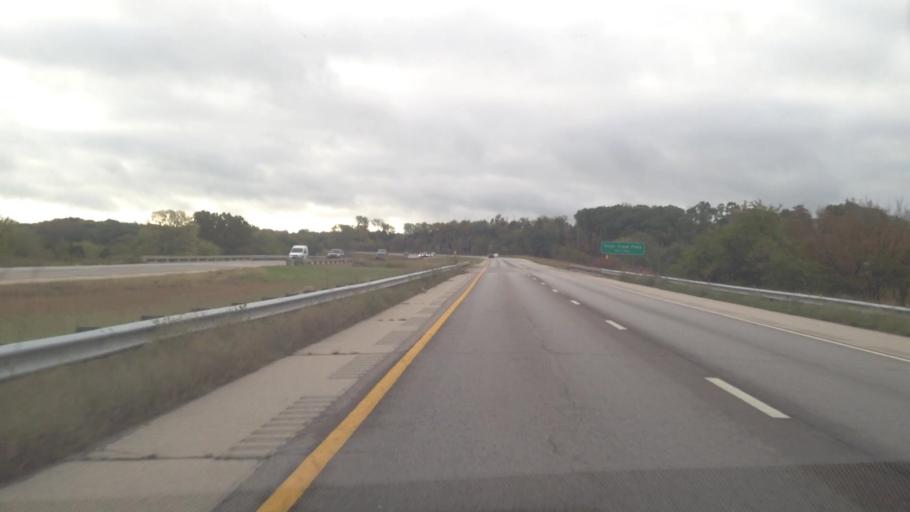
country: US
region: Kansas
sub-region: Johnson County
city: De Soto
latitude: 38.9511
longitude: -94.9061
